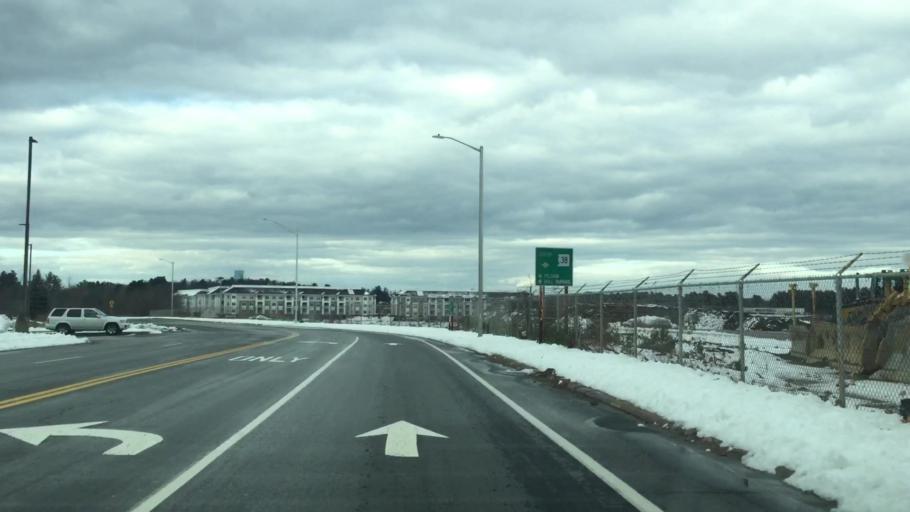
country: US
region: New Hampshire
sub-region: Rockingham County
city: Salem
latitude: 42.7712
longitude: -71.2303
